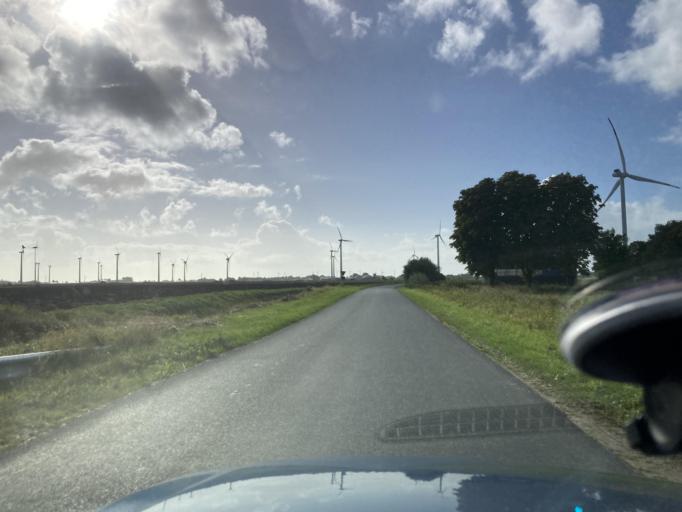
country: DE
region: Schleswig-Holstein
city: Norderwohrden
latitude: 54.1789
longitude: 9.0360
